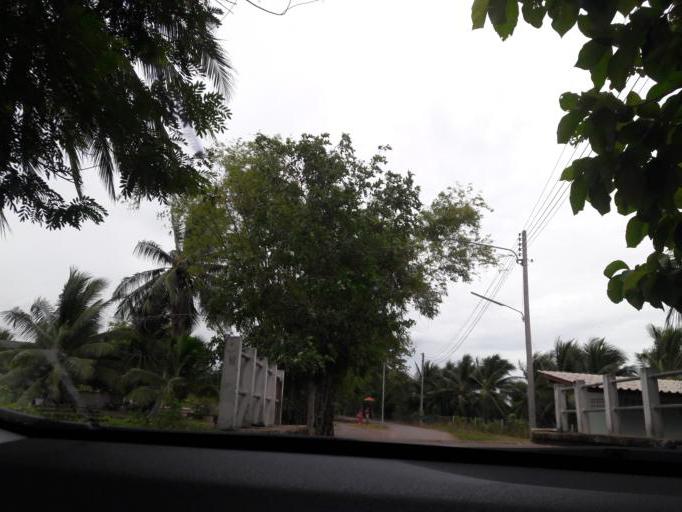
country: TH
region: Samut Sakhon
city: Ban Phaeo
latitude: 13.5482
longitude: 100.0412
